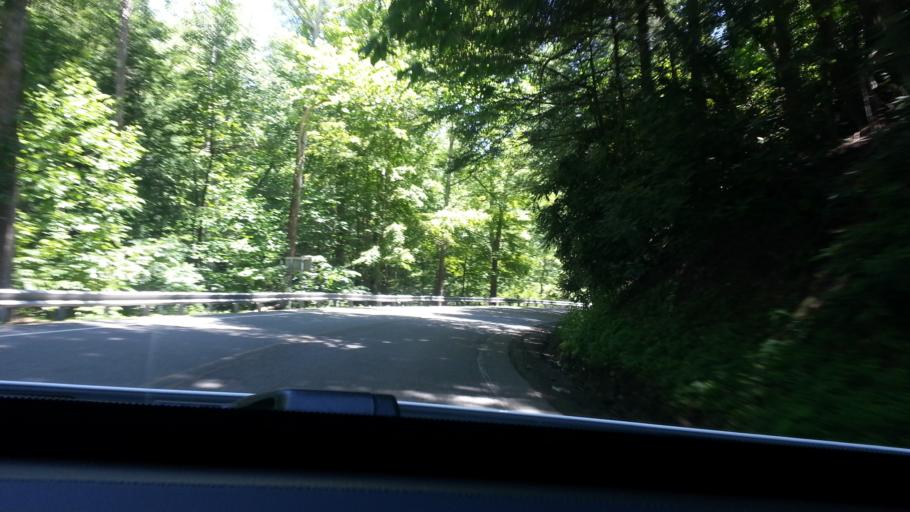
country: US
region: West Virginia
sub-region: Fayette County
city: Ansted
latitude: 38.1002
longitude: -81.1526
